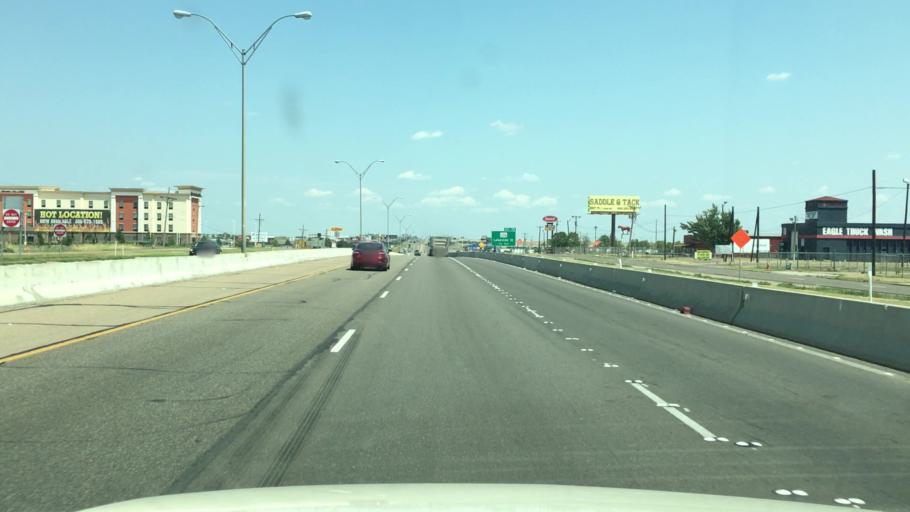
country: US
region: Texas
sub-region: Potter County
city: Amarillo
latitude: 35.1926
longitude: -101.7553
